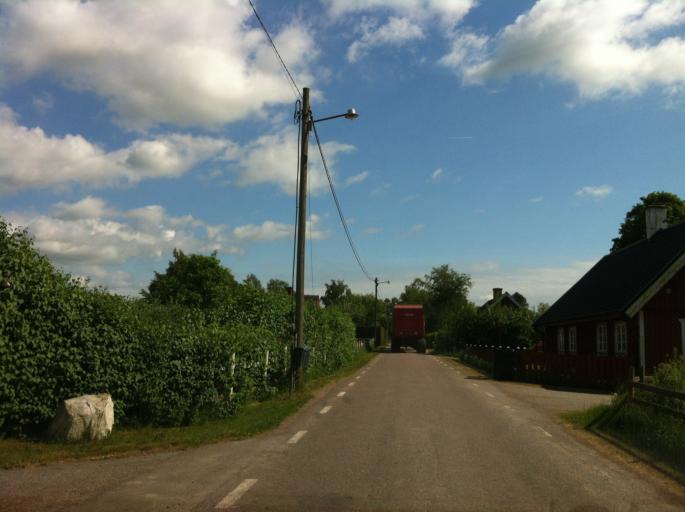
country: SE
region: Skane
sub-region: Landskrona
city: Asmundtorp
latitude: 55.9463
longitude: 12.9158
